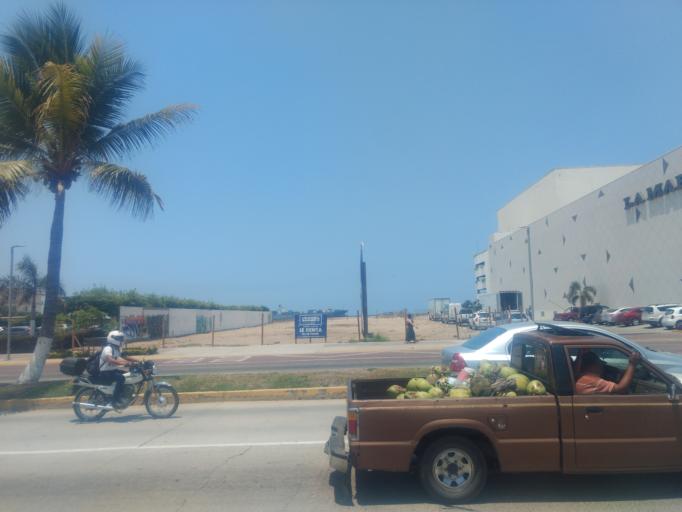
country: MX
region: Colima
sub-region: Manzanillo
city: Manzanillo
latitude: 19.1000
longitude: -104.3245
